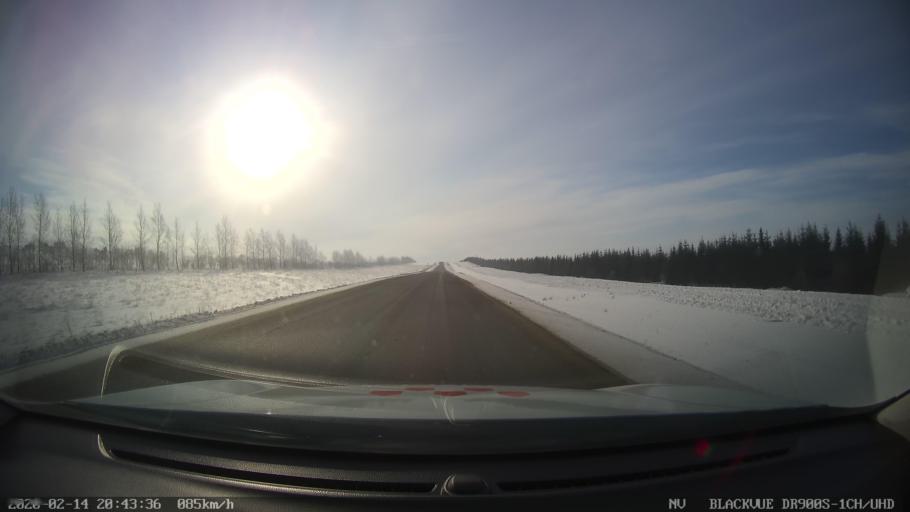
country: RU
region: Tatarstan
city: Kuybyshevskiy Zaton
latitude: 55.3061
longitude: 49.1484
